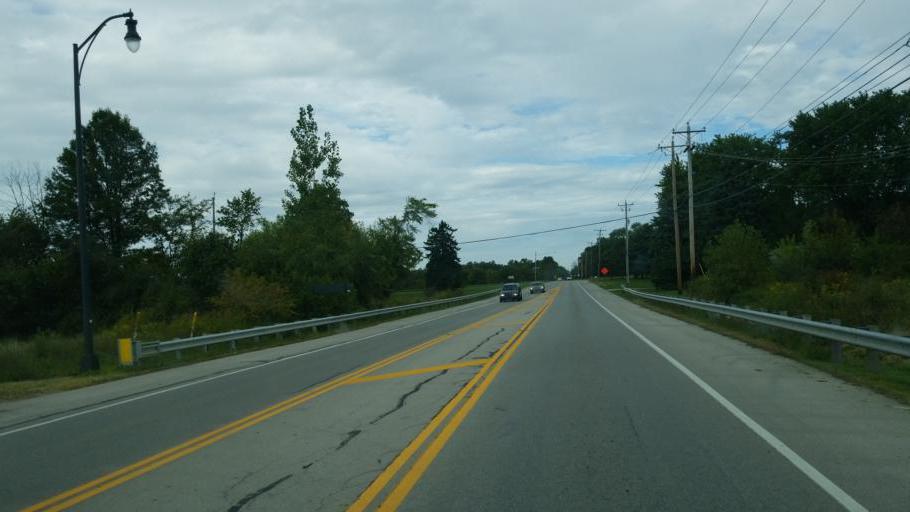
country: US
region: Ohio
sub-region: Franklin County
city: New Albany
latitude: 40.1067
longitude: -82.8116
